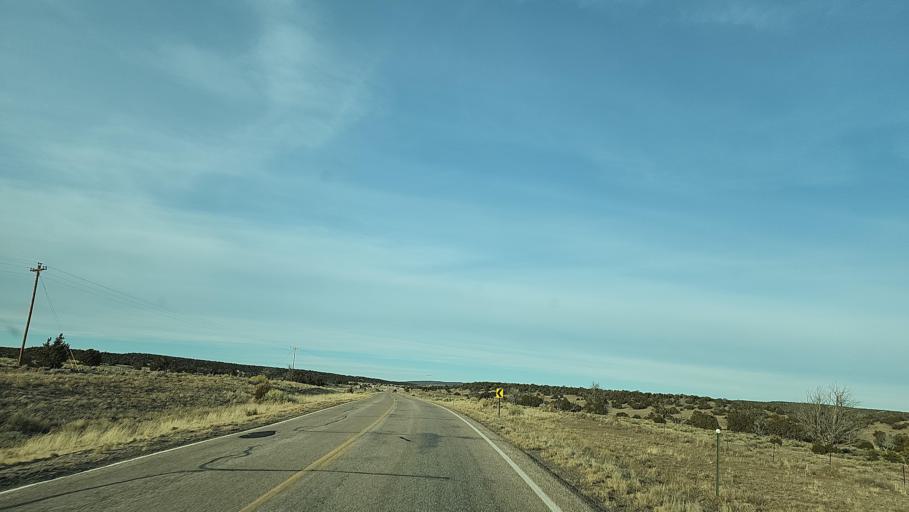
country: US
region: New Mexico
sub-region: Catron County
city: Reserve
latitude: 34.3887
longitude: -108.4494
